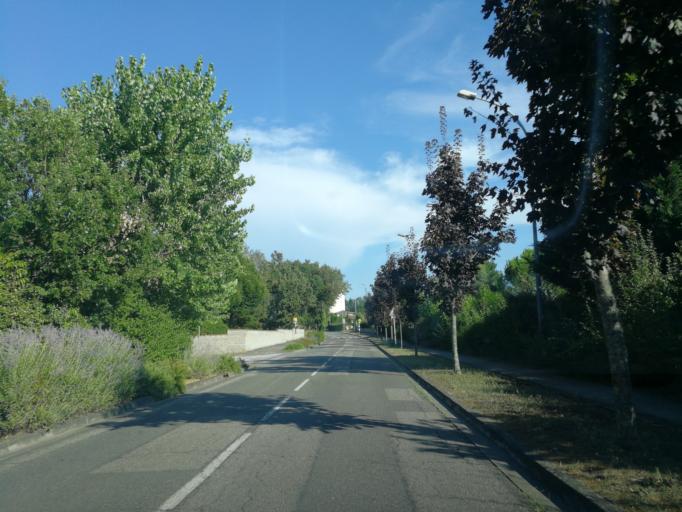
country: FR
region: Midi-Pyrenees
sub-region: Departement de la Haute-Garonne
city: Balma
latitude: 43.6176
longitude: 1.5196
